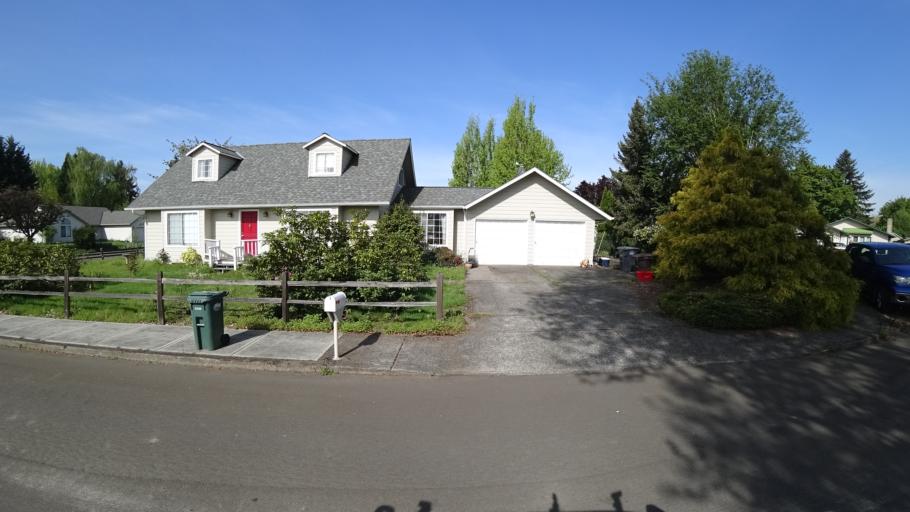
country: US
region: Oregon
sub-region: Washington County
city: Hillsboro
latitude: 45.5269
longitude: -122.9555
